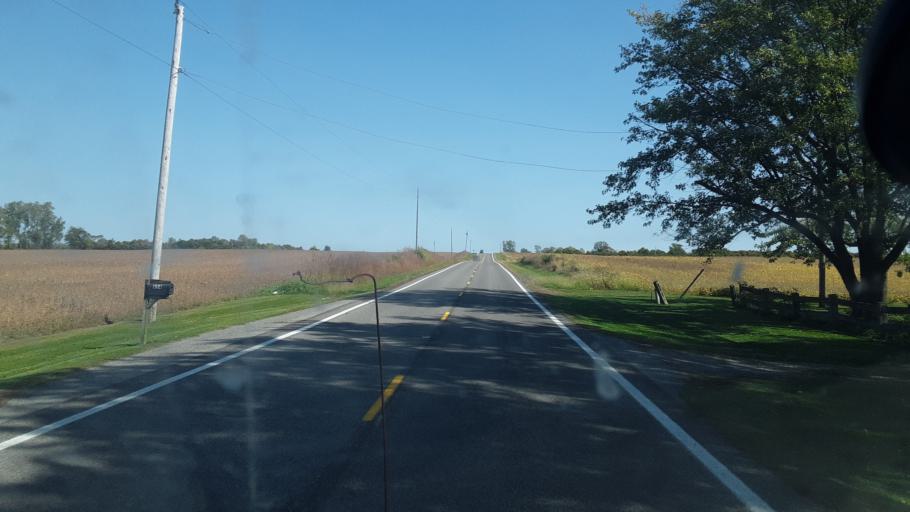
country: US
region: Ohio
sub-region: Logan County
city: Northwood
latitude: 40.5052
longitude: -83.6832
